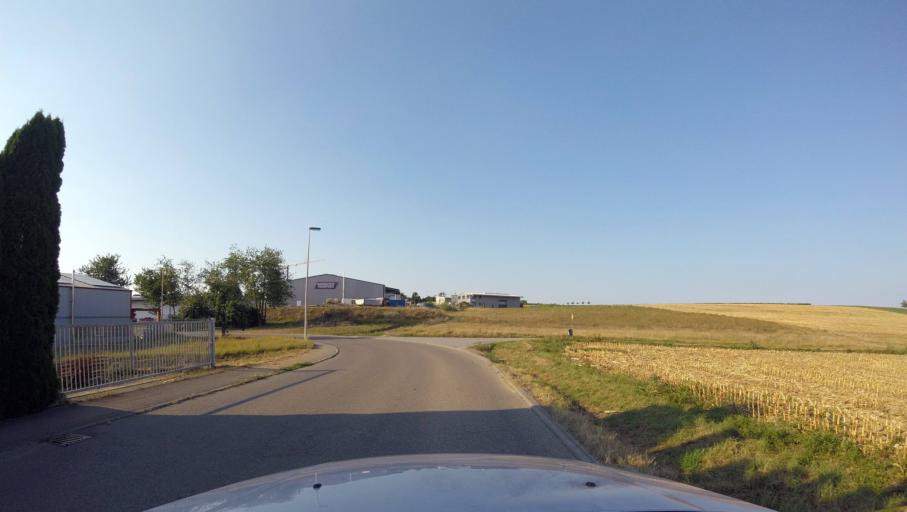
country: DE
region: Baden-Wuerttemberg
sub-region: Regierungsbezirk Stuttgart
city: Mittelschontal
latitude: 48.9224
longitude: 9.3975
